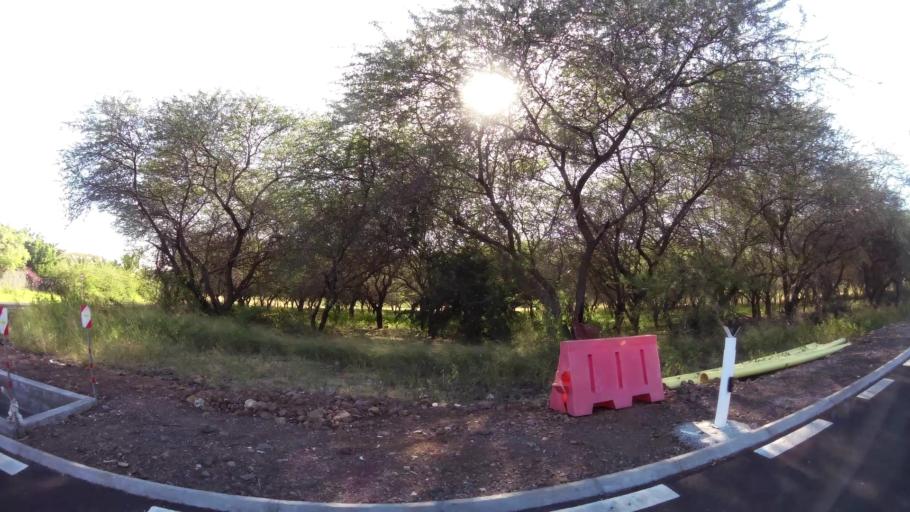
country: MU
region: Black River
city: Tamarin
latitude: -20.3366
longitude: 57.3819
